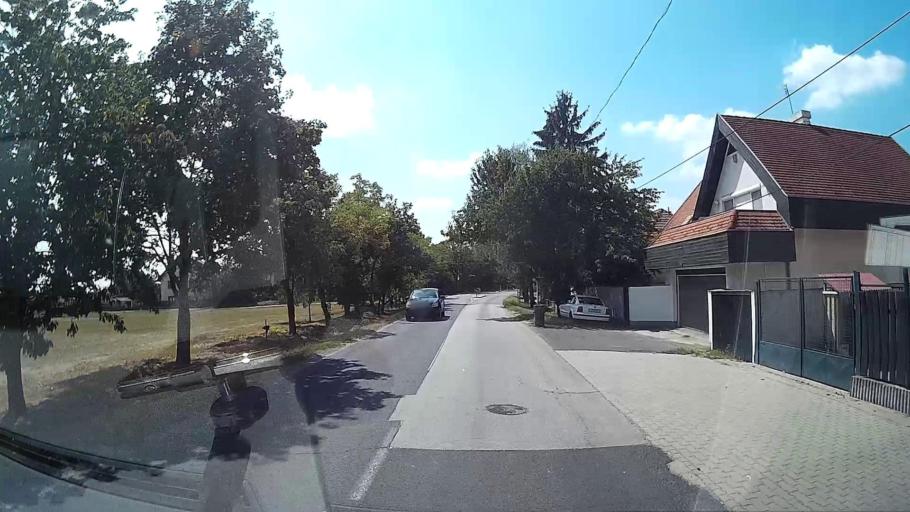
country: HU
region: Pest
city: Budakalasz
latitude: 47.6299
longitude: 19.0589
